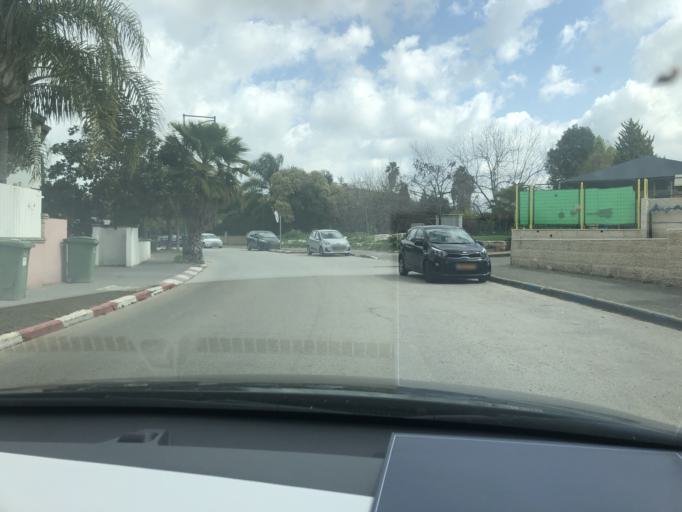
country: IL
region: Haifa
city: Hadera
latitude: 32.4667
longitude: 34.9566
